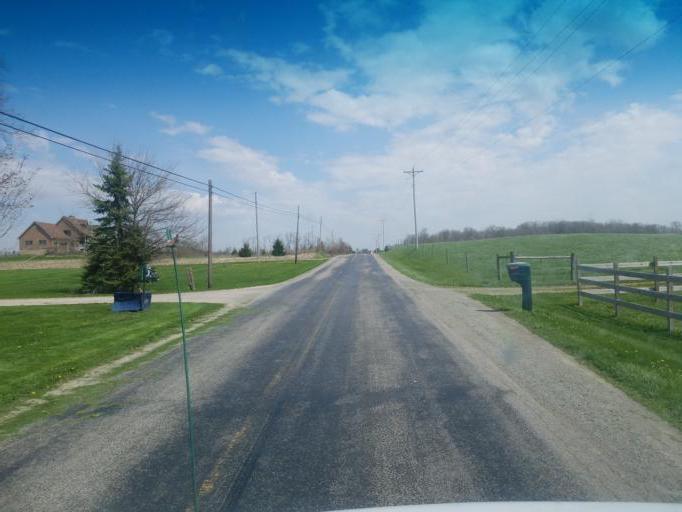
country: US
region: Ohio
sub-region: Hardin County
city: Kenton
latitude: 40.5928
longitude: -83.6738
